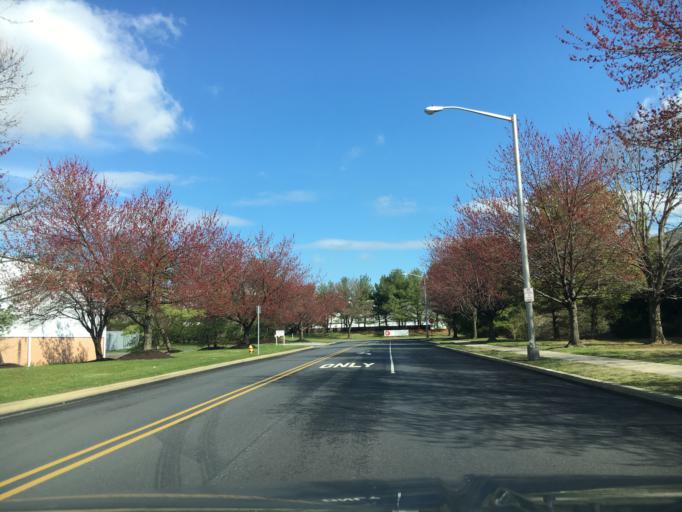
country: US
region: Pennsylvania
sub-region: Northampton County
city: Bath
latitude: 40.6781
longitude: -75.3829
